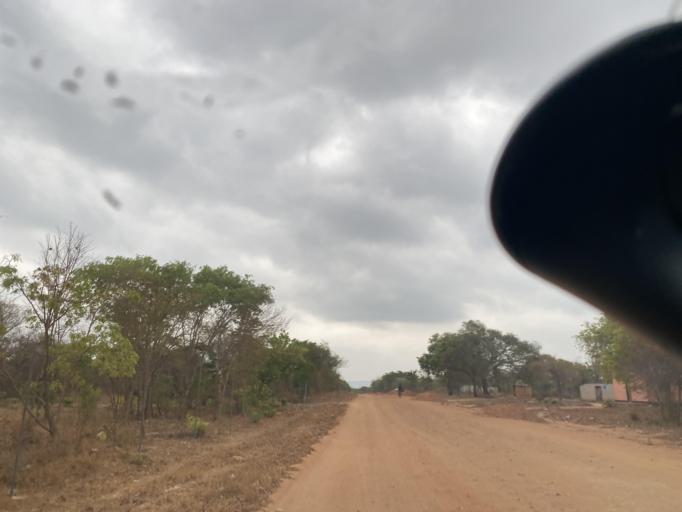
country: ZM
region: Lusaka
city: Chongwe
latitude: -15.2729
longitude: 28.7312
